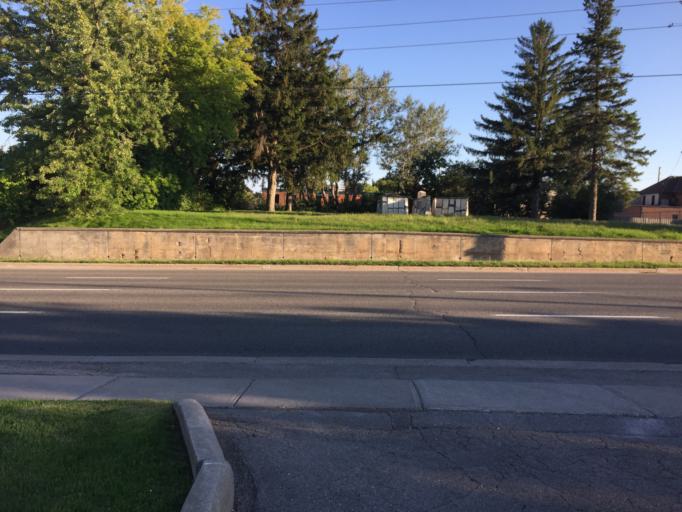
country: CA
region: Ontario
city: Oshawa
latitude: 43.8970
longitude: -78.8713
